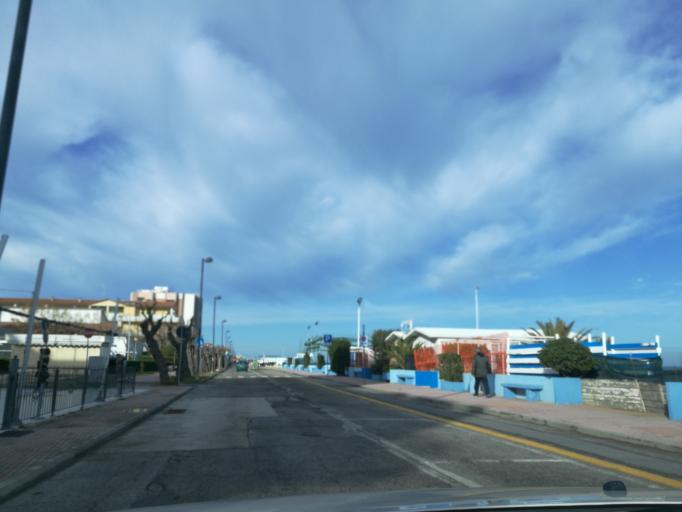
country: IT
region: The Marches
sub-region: Provincia di Pesaro e Urbino
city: Marotta
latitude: 43.7770
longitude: 13.1275
